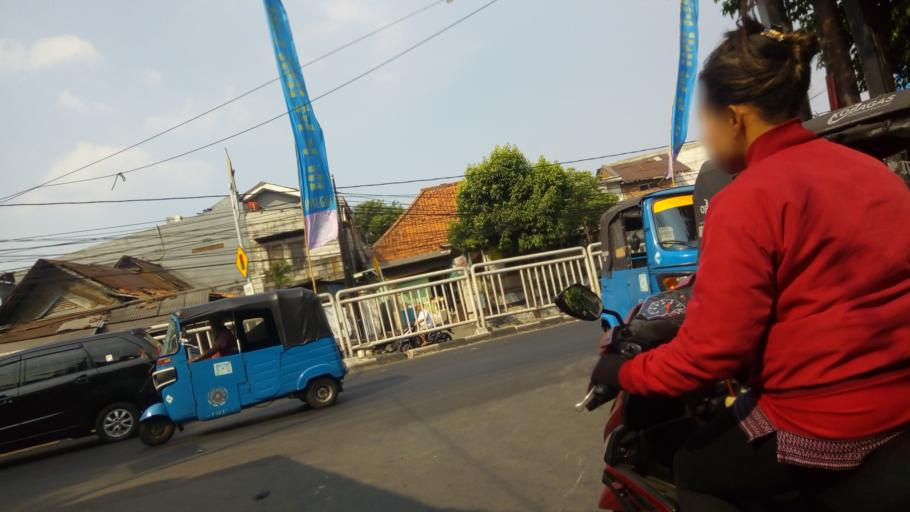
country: ID
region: Jakarta Raya
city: Jakarta
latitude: -6.2188
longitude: 106.8450
